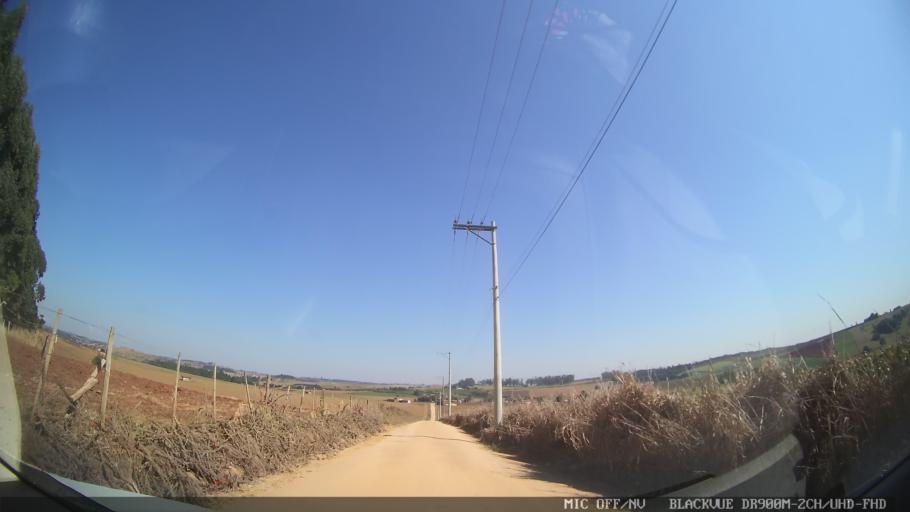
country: BR
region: Sao Paulo
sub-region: Itupeva
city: Itupeva
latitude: -23.1219
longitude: -47.0674
